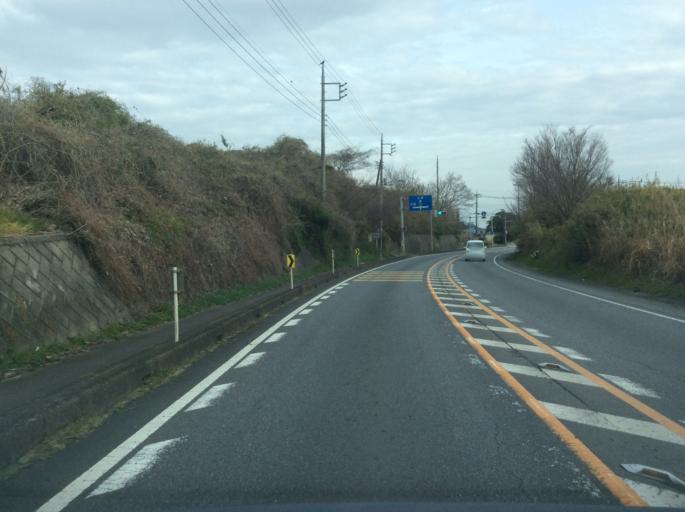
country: JP
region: Ibaraki
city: Tsukuba
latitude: 36.1531
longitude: 140.1161
